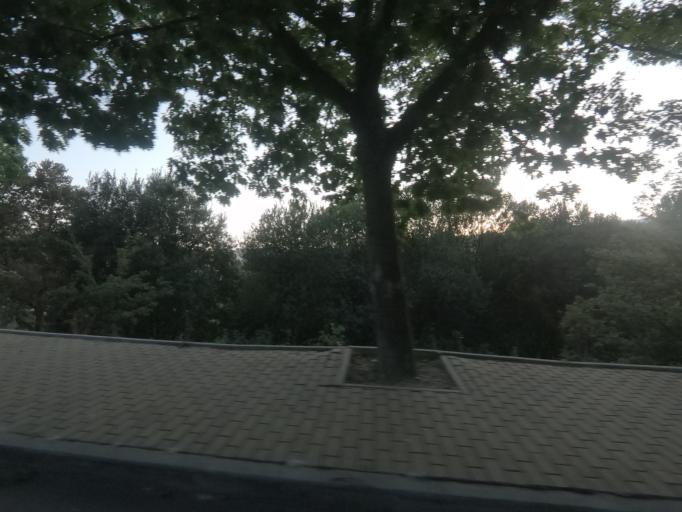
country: PT
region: Vila Real
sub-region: Vila Real
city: Vila Real
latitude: 41.3025
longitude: -7.7310
